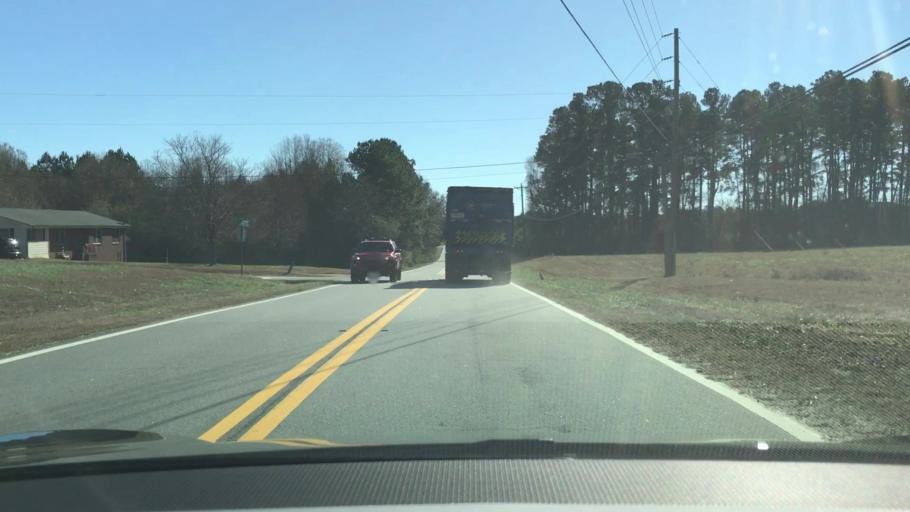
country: US
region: Georgia
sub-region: Barrow County
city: Auburn
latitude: 33.9305
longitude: -83.8302
